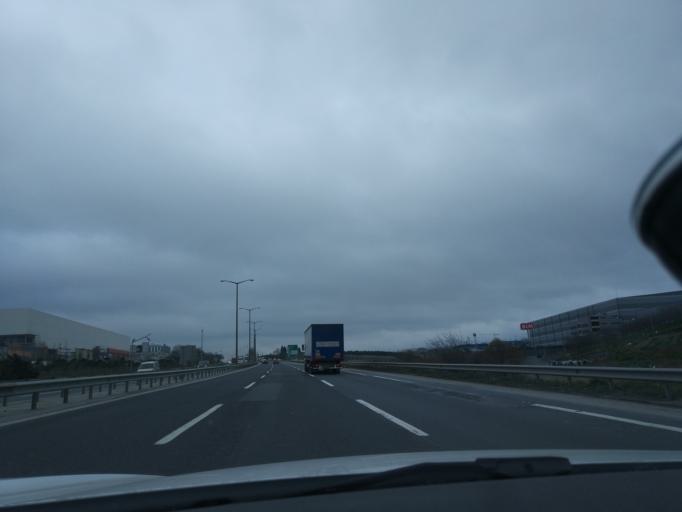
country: TR
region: Istanbul
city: Esenyurt
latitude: 41.0743
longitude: 28.6471
